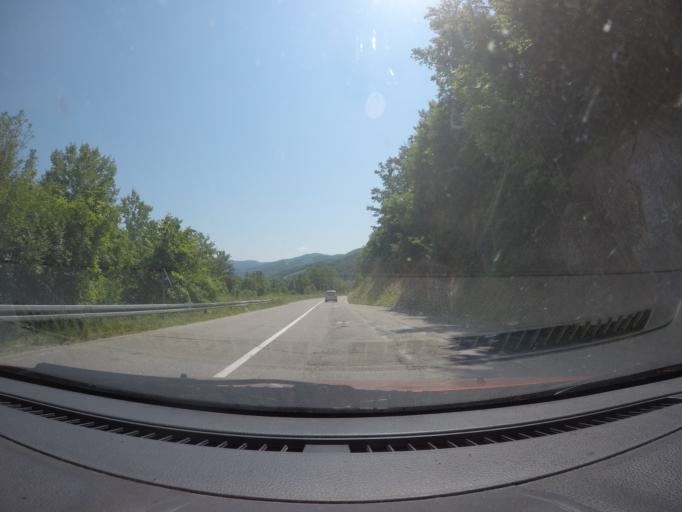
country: RO
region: Mehedinti
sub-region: Comuna Eselnita
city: Eselnita
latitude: 44.6656
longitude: 22.3439
